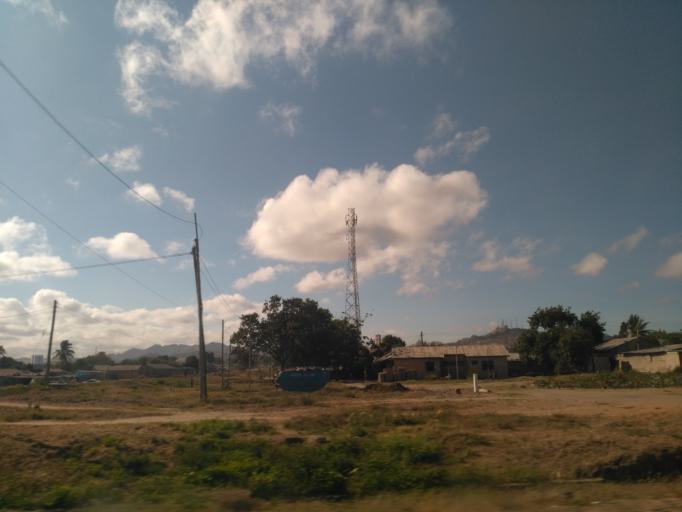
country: TZ
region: Dodoma
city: Dodoma
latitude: -6.1776
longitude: 35.7362
